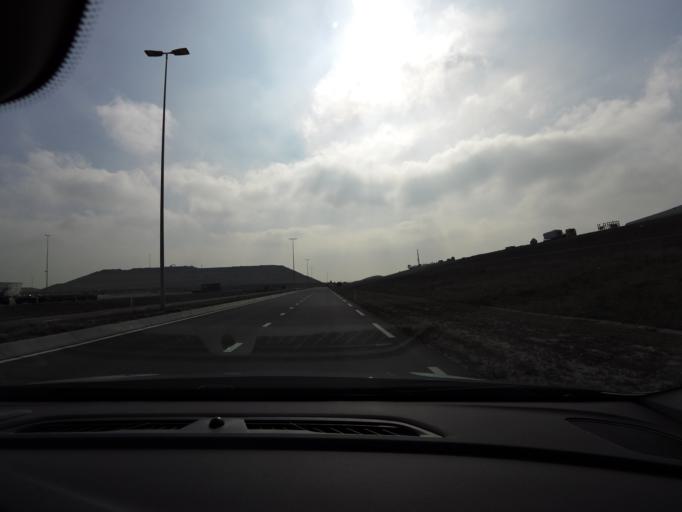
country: NL
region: South Holland
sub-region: Gemeente Goeree-Overflakkee
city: Goedereede
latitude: 51.9299
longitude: 4.0182
